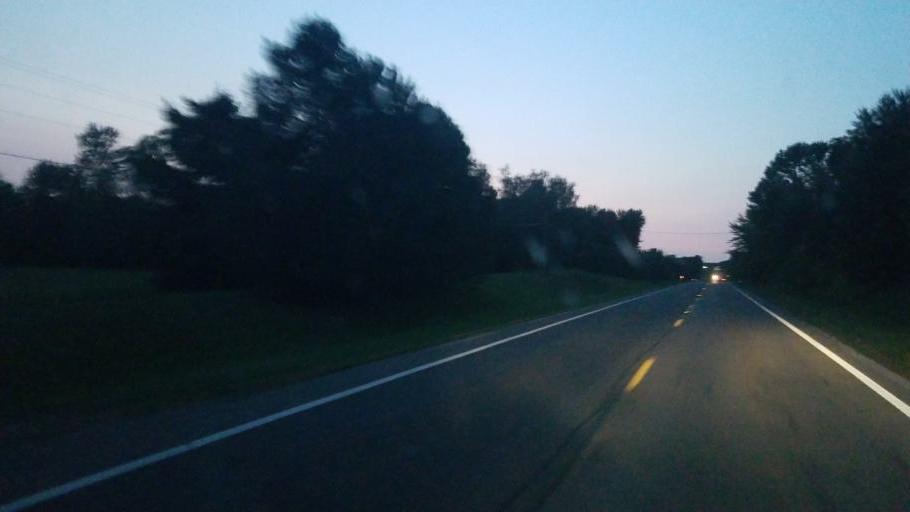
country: US
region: Ohio
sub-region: Morrow County
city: Mount Gilead
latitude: 40.5180
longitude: -82.7474
